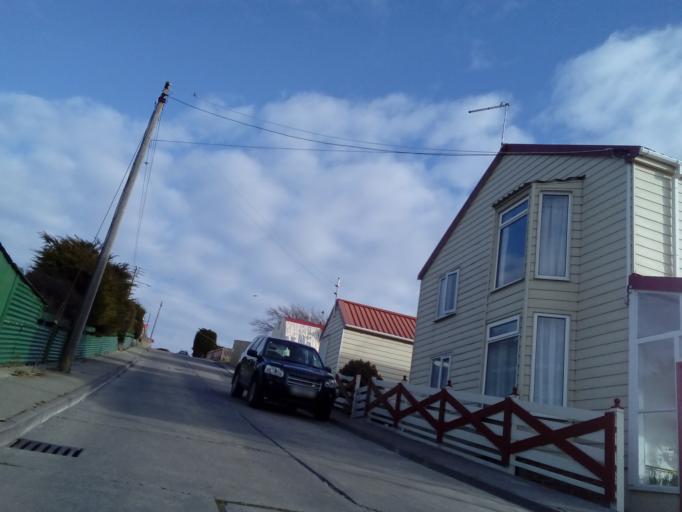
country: FK
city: Stanley
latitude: -51.6928
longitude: -57.8666
